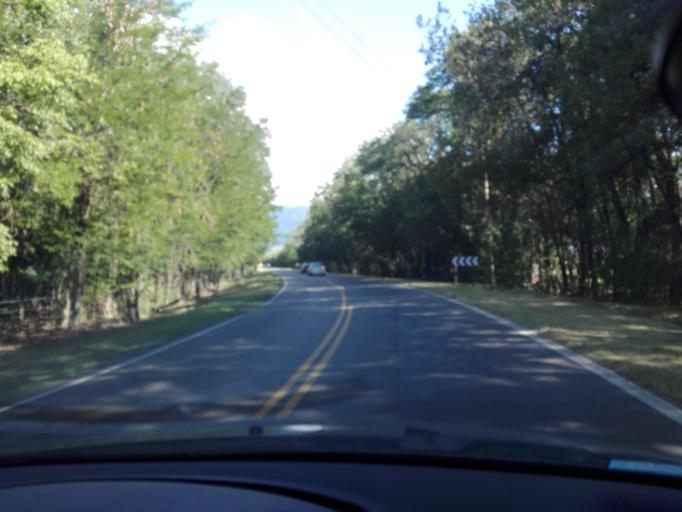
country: AR
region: Cordoba
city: Mina Clavero
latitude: -31.8240
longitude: -64.9996
